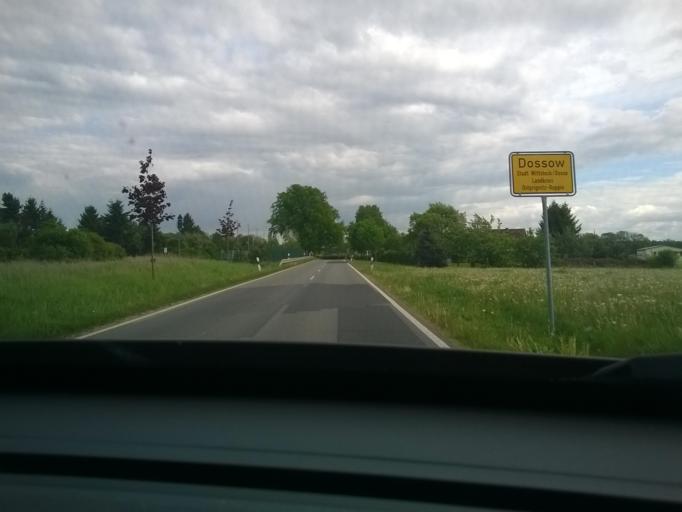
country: DE
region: Brandenburg
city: Wittstock
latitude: 53.1218
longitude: 12.5197
